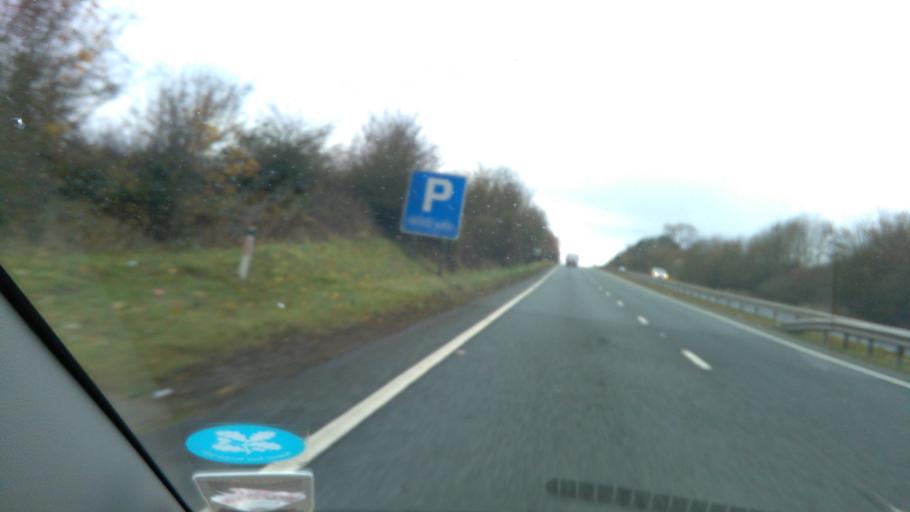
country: GB
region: England
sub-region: Northamptonshire
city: Blisworth
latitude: 52.1746
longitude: -0.9566
